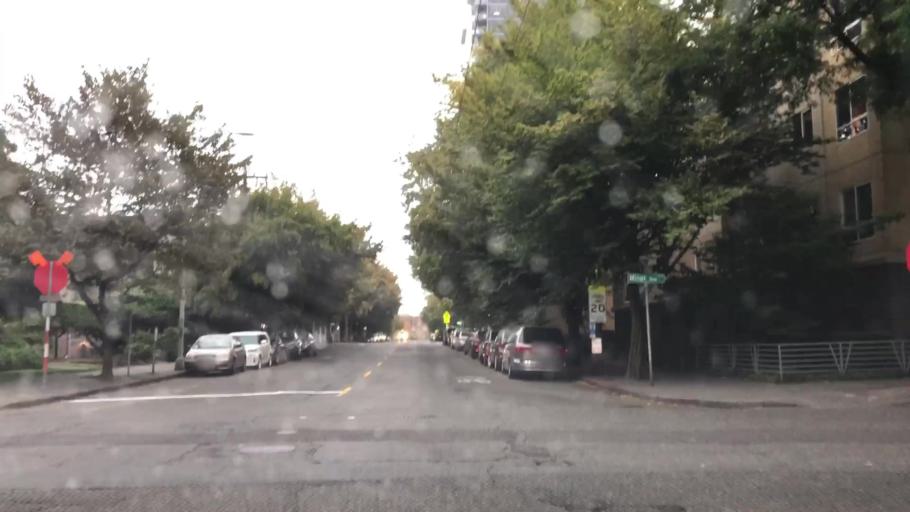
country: US
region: Washington
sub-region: Kitsap County
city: Bainbridge Island
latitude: 47.5789
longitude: -122.4949
